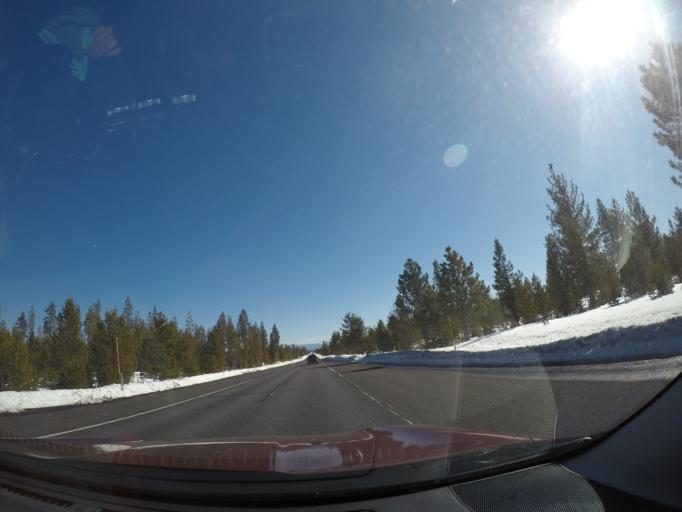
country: US
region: Oregon
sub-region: Deschutes County
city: Three Rivers
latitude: 43.8896
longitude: -121.5846
